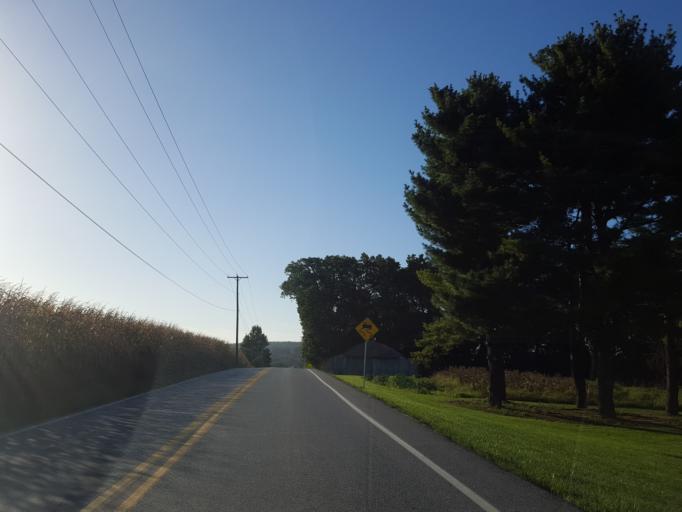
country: US
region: Pennsylvania
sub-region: York County
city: Stonybrook
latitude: 39.9652
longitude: -76.6132
